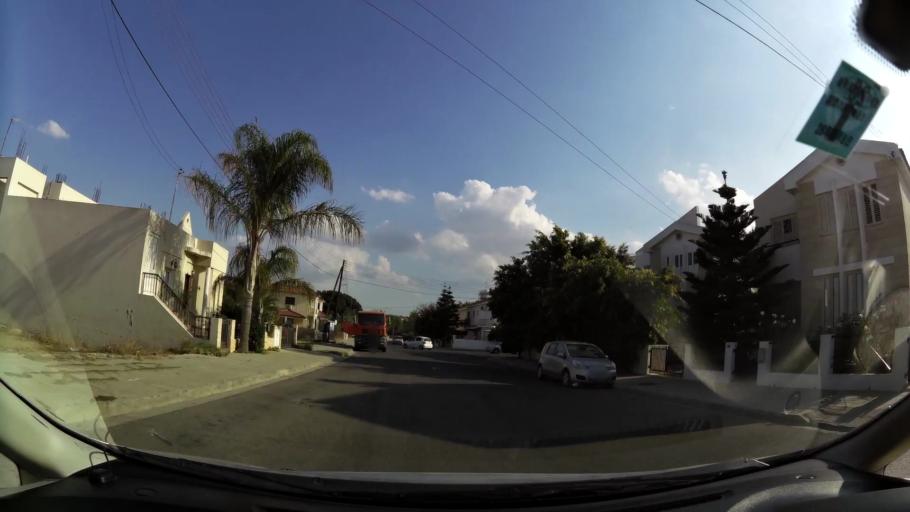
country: CY
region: Lefkosia
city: Kato Deftera
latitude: 35.1223
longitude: 33.3007
